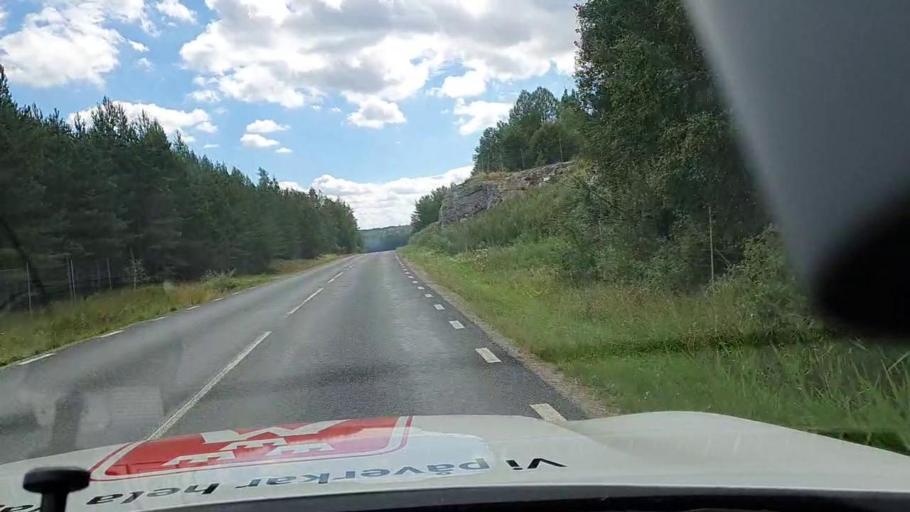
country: SE
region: Soedermanland
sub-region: Nykopings Kommun
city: Olstorp
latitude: 58.7540
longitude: 16.6162
